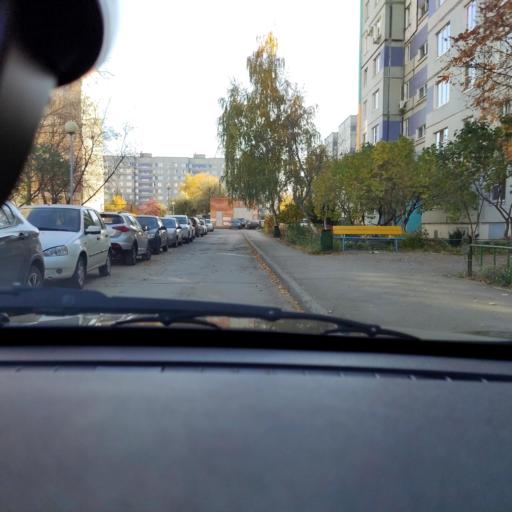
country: RU
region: Samara
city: Tol'yatti
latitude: 53.5389
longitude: 49.3405
